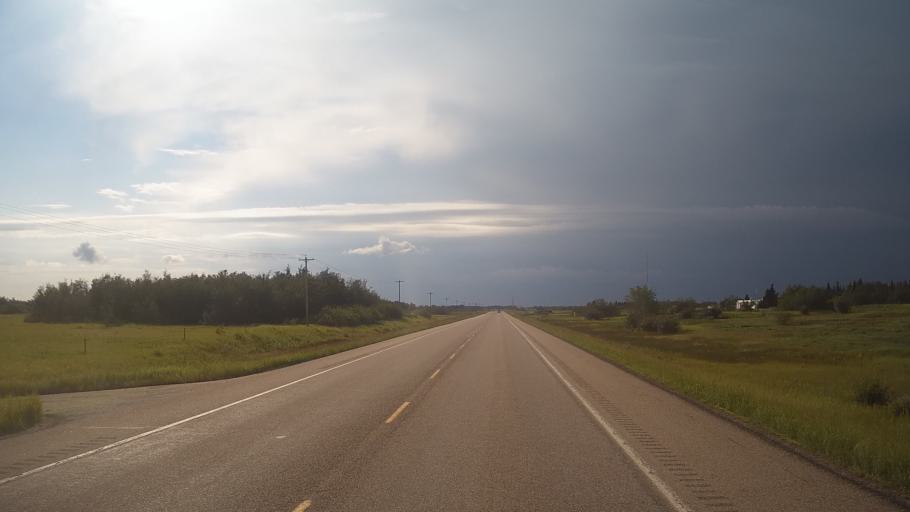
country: CA
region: Alberta
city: Viking
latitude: 53.1686
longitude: -112.0332
